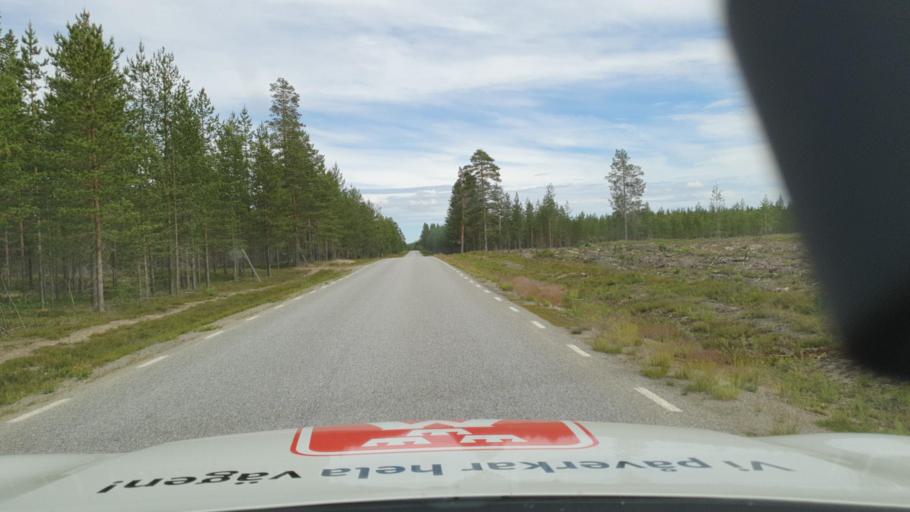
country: SE
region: Vaesterbotten
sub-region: Skelleftea Kommun
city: Burtraesk
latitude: 64.5048
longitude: 20.8088
